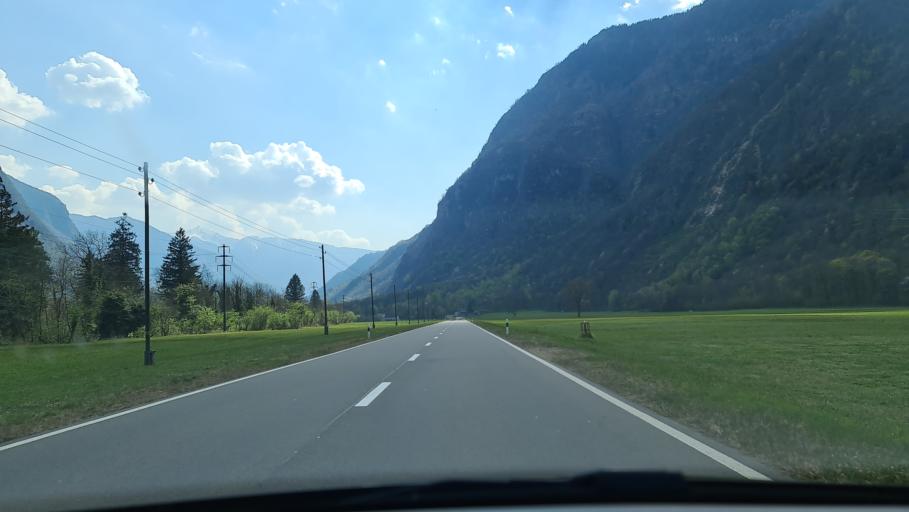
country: CH
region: Grisons
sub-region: Moesa District
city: Santa Maria in Calanca
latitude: 46.3020
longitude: 9.1876
